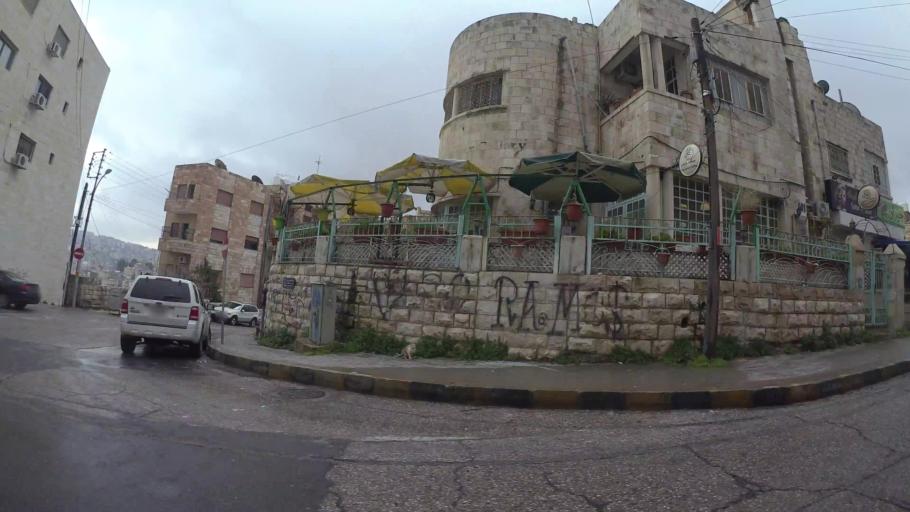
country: JO
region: Amman
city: Amman
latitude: 31.9482
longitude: 35.9228
